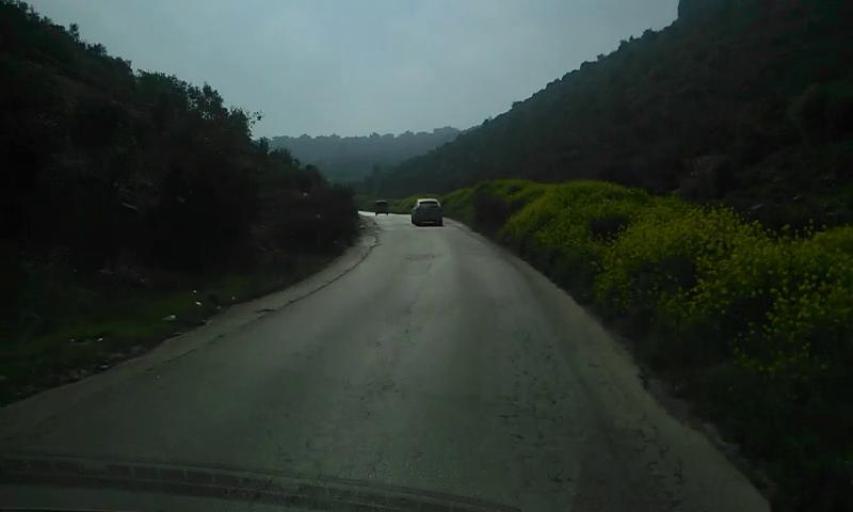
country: PS
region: West Bank
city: `Ayn Yabrud
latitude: 31.9527
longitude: 35.2393
